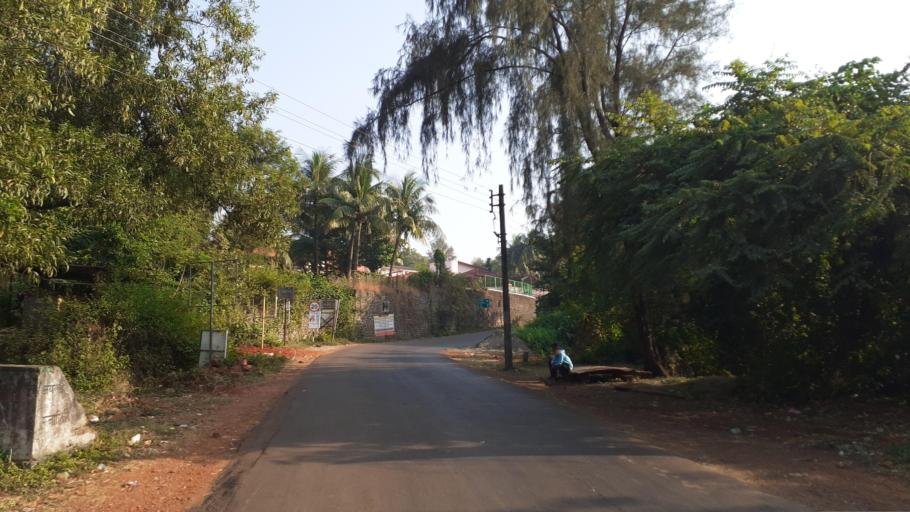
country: IN
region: Maharashtra
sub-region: Ratnagiri
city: Ratnagiri
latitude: 17.1438
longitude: 73.2693
